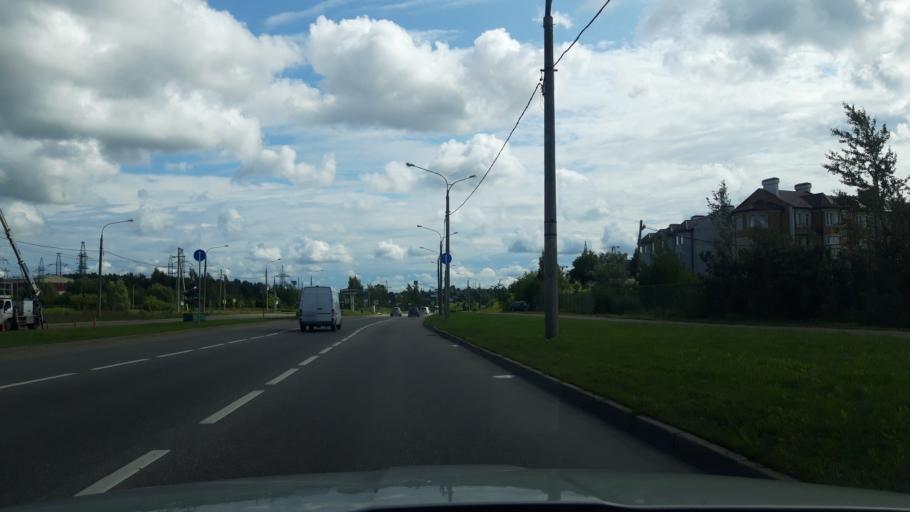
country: RU
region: Moscow
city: Zelenograd
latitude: 55.9600
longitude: 37.1862
